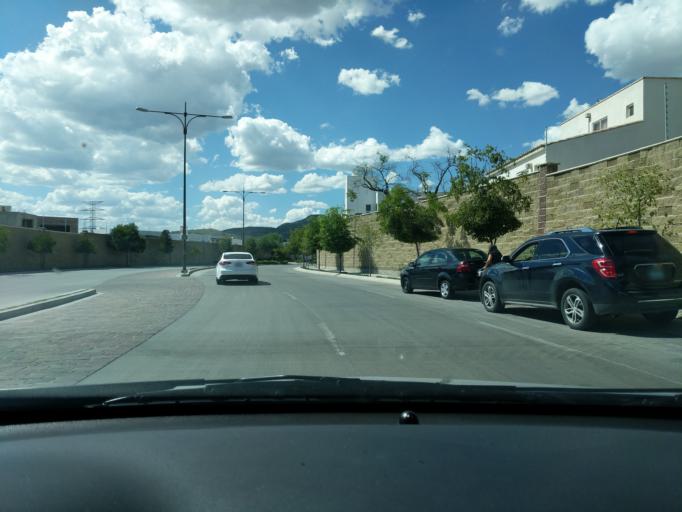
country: MX
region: Guanajuato
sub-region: Leon
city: Medina
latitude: 21.1318
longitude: -101.6044
